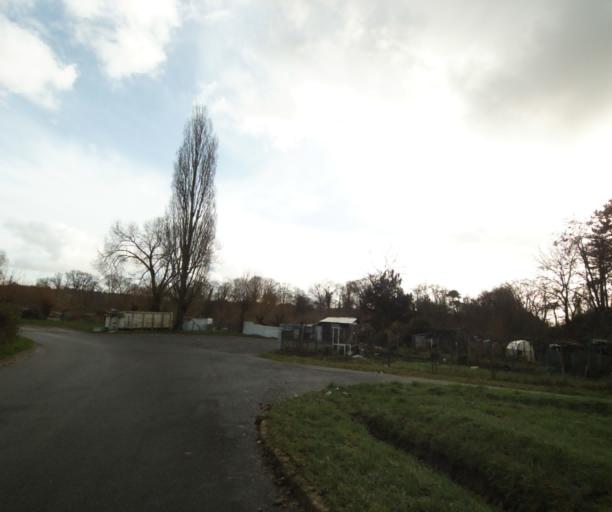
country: FR
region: Pays de la Loire
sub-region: Departement de la Sarthe
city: Le Mans
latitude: 47.9896
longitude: 0.2276
